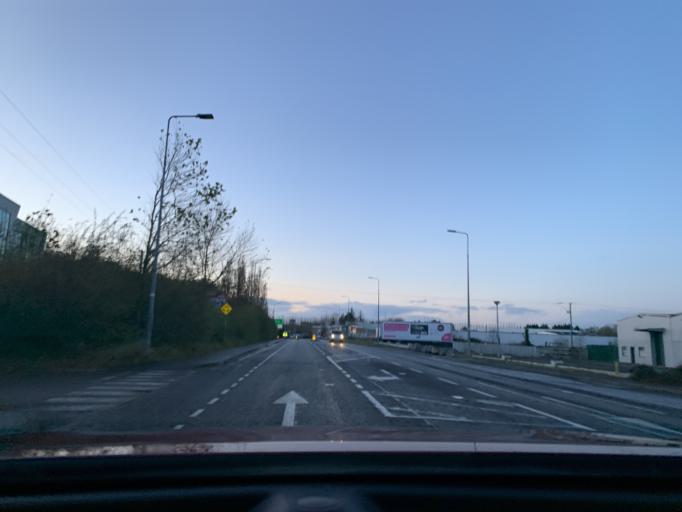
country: IE
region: Connaught
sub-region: County Leitrim
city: Carrick-on-Shannon
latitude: 53.9443
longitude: -8.0726
